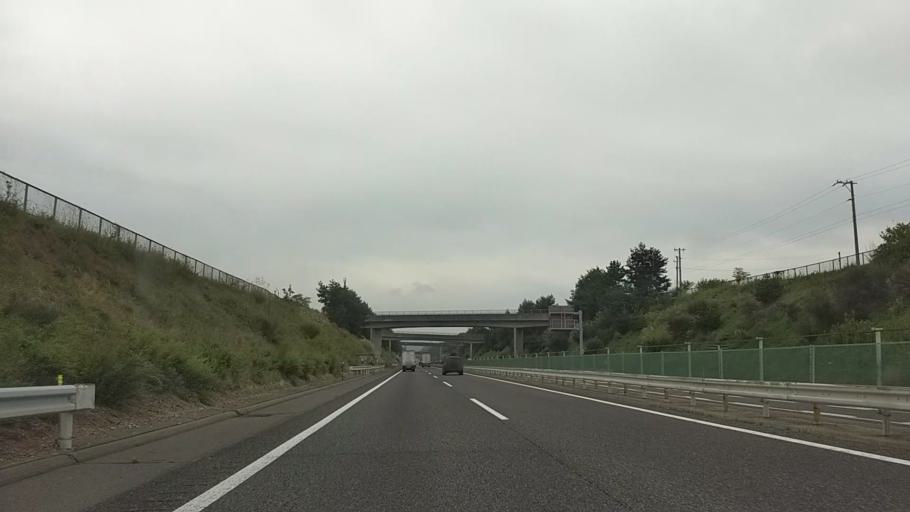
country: JP
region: Nagano
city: Shiojiri
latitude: 36.1264
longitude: 137.9764
